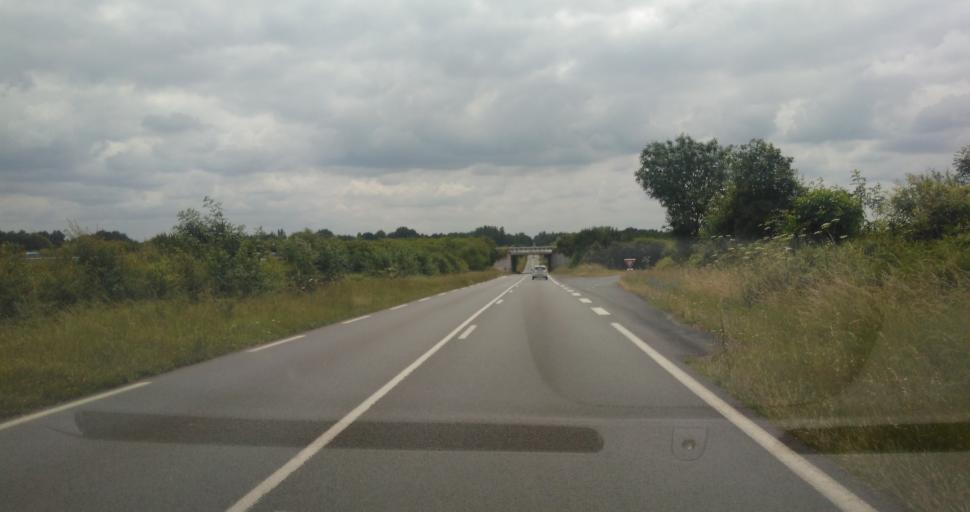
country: FR
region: Pays de la Loire
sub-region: Departement de la Vendee
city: Bournezeau
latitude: 46.6074
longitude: -1.1410
